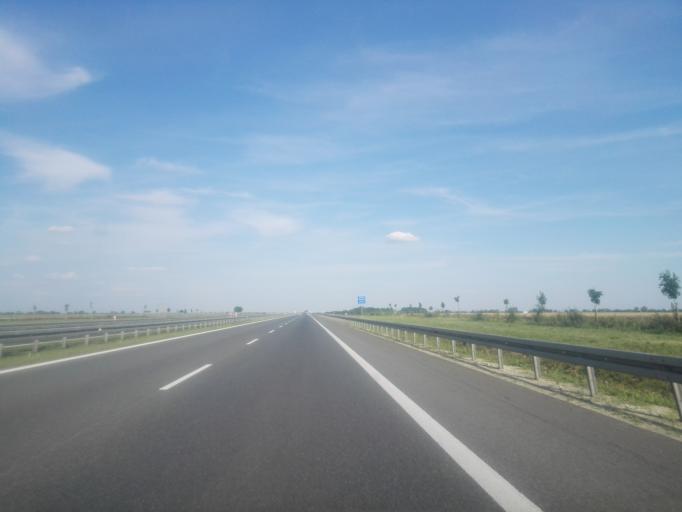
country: PL
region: Lower Silesian Voivodeship
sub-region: Powiat olesnicki
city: Dobroszyce
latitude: 51.2238
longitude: 17.2964
